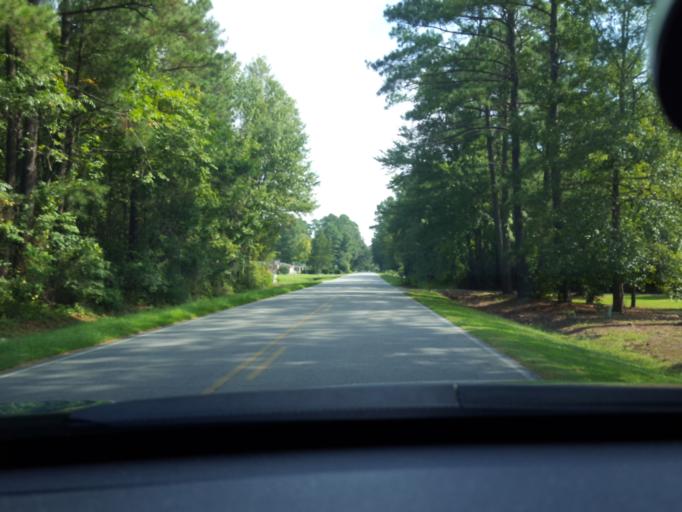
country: US
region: North Carolina
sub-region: Washington County
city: Plymouth
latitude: 35.8718
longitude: -76.7237
